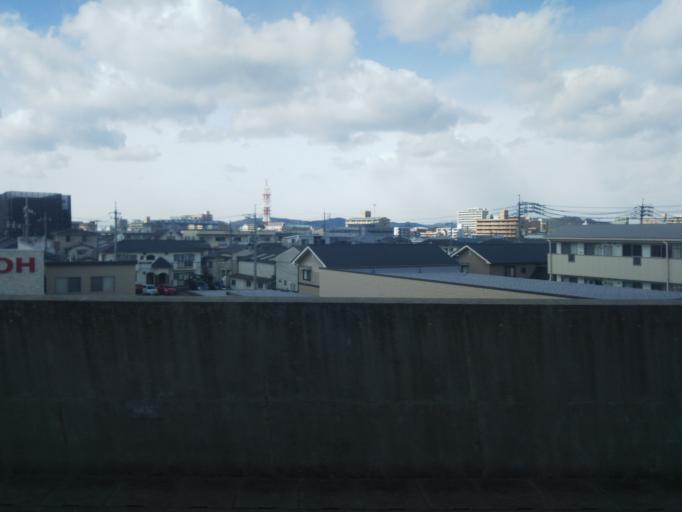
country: JP
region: Okayama
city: Okayama-shi
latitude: 34.6363
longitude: 133.9046
